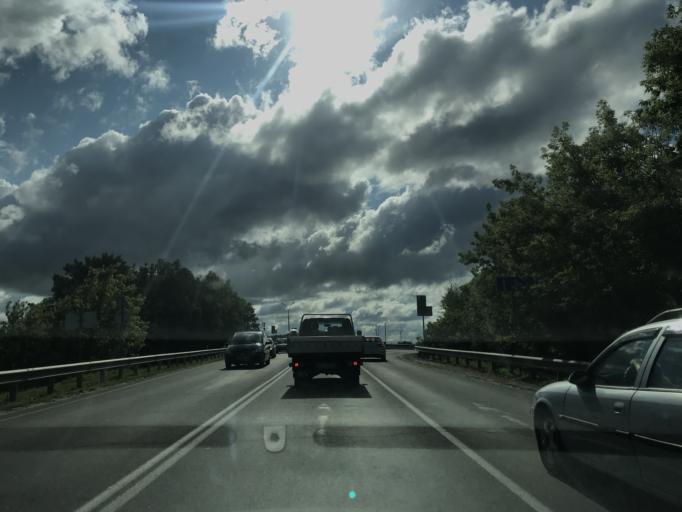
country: BY
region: Minsk
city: Borovlyany
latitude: 53.9670
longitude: 27.6408
